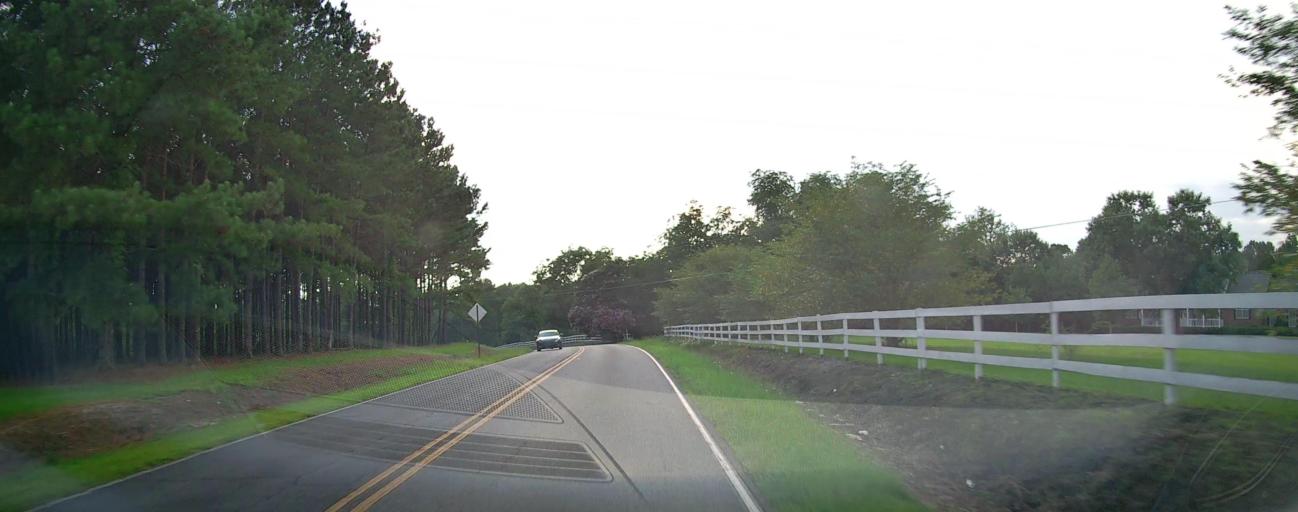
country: US
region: Georgia
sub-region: Peach County
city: Byron
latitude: 32.7238
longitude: -83.7603
